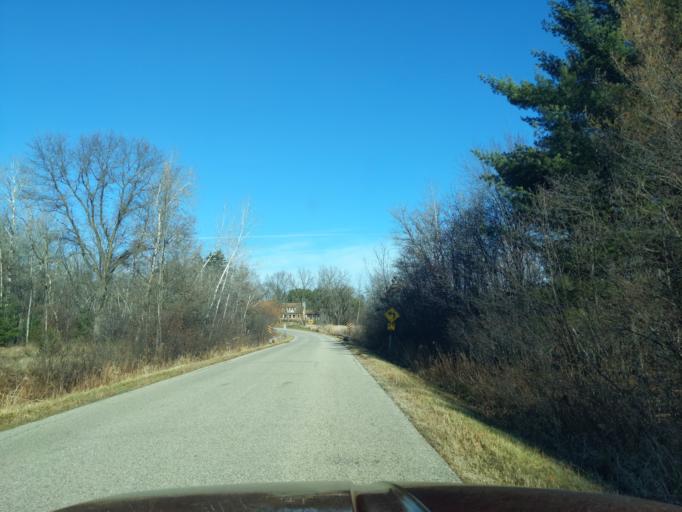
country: US
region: Wisconsin
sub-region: Waushara County
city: Silver Lake
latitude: 44.0616
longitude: -89.1887
